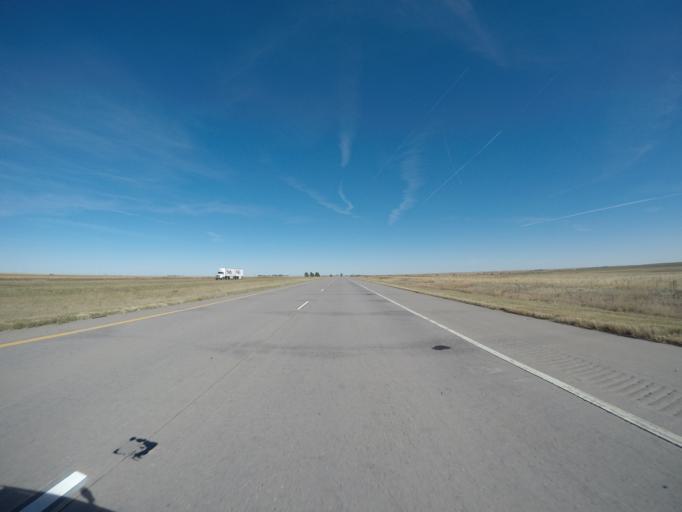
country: US
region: Colorado
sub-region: Kit Carson County
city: Burlington
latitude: 39.3255
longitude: -102.0982
